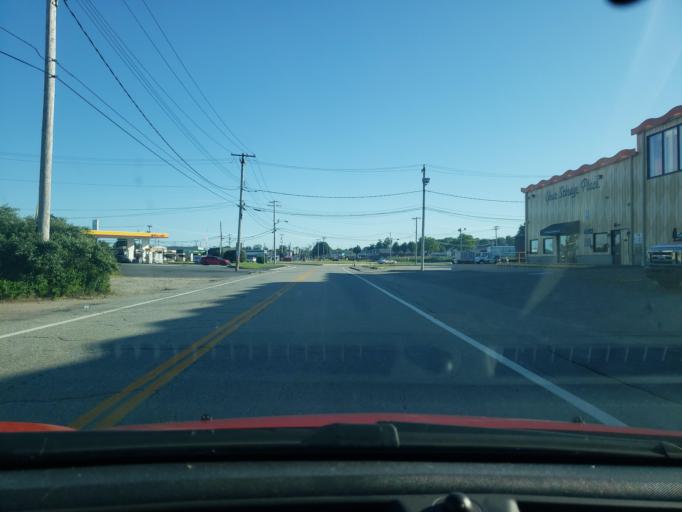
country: US
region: Rhode Island
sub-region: Newport County
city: Newport
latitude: 41.5055
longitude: -71.3176
